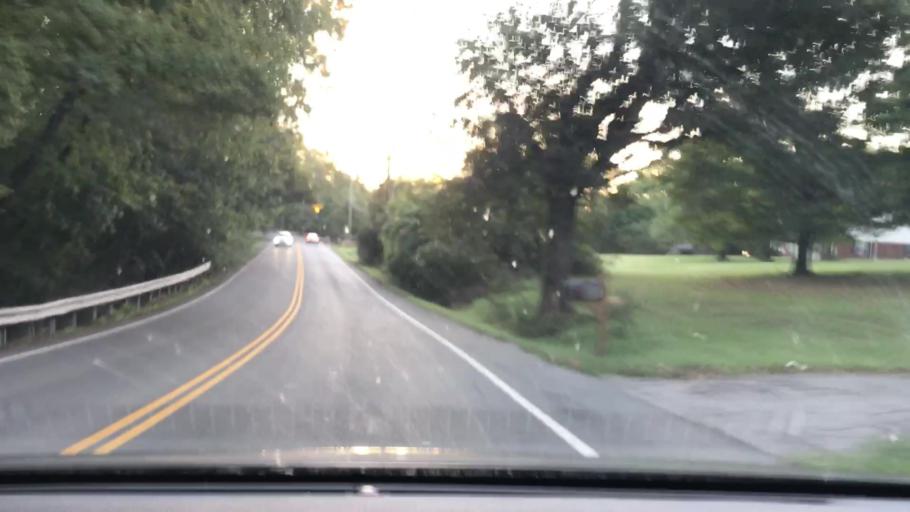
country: US
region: Tennessee
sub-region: Davidson County
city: Oak Hill
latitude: 36.0682
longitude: -86.7058
